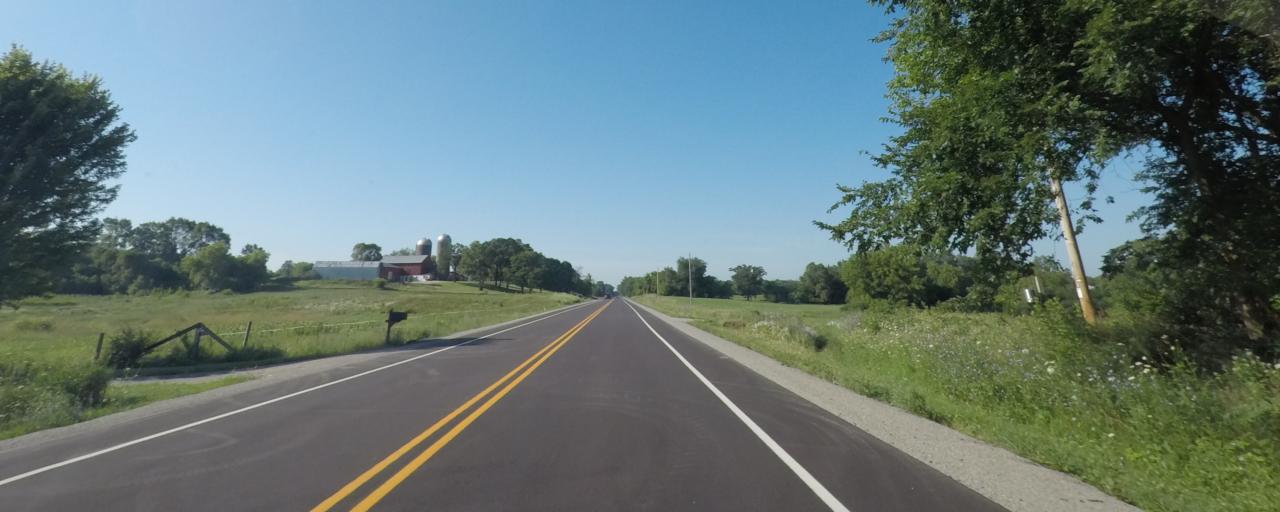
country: US
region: Wisconsin
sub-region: Jefferson County
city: Palmyra
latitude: 42.9260
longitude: -88.5864
